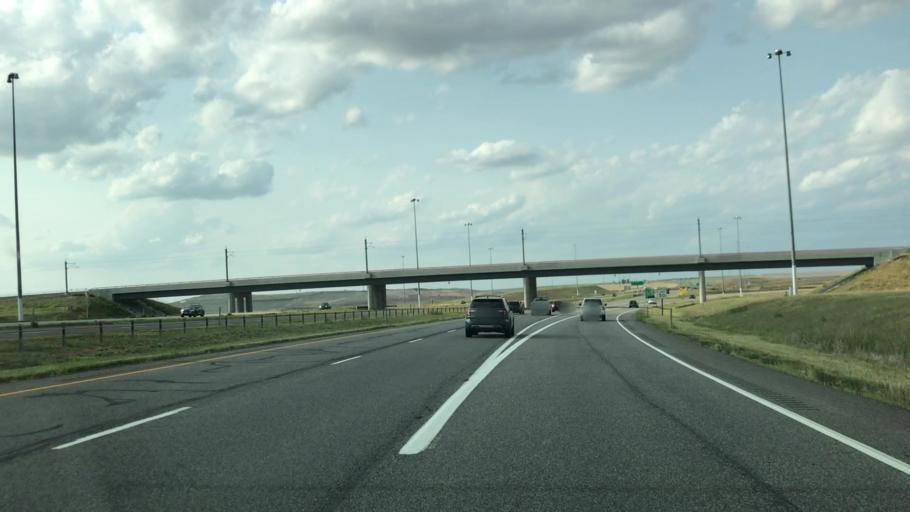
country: US
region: Colorado
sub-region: Adams County
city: Aurora
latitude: 39.8260
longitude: -104.7467
